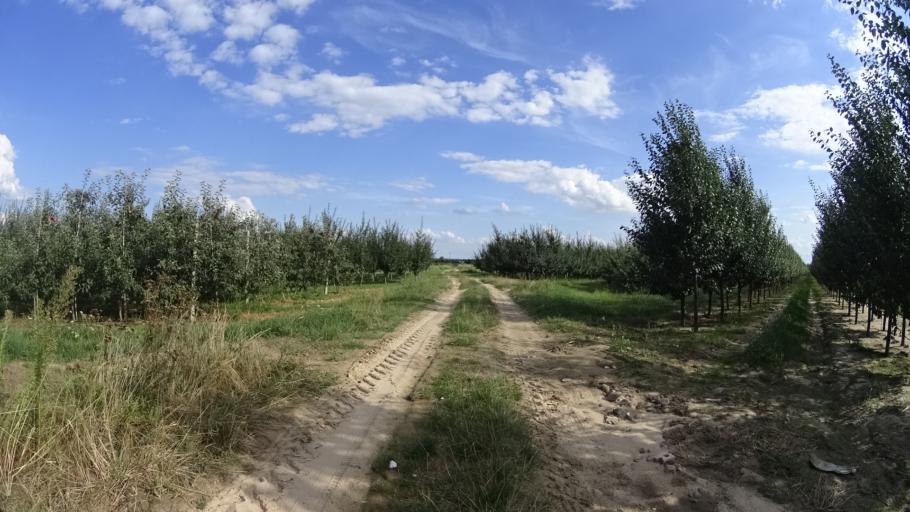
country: PL
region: Masovian Voivodeship
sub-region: Powiat bialobrzeski
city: Wysmierzyce
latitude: 51.6658
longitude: 20.8123
